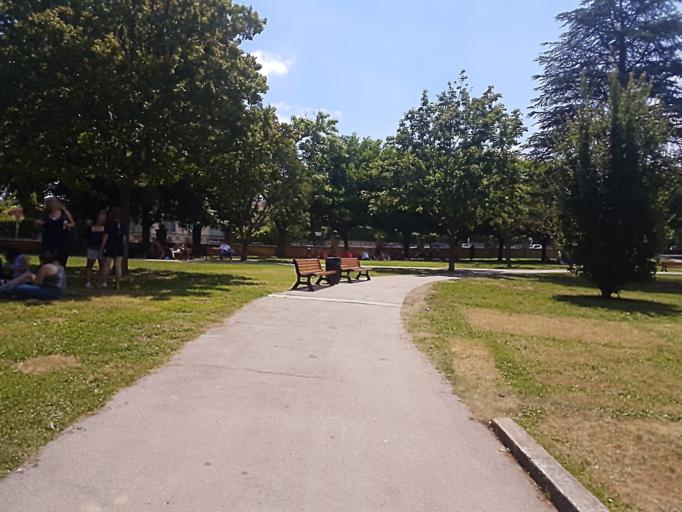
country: FR
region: Provence-Alpes-Cote d'Azur
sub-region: Departement des Bouches-du-Rhone
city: Aix-en-Provence
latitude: 43.5211
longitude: 5.4490
